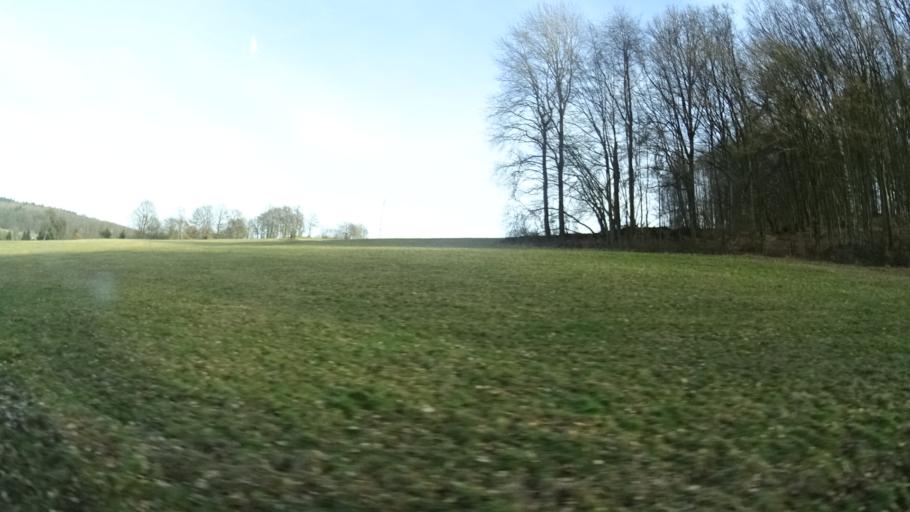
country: DE
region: Bavaria
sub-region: Regierungsbezirk Unterfranken
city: Bad Bruckenau
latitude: 50.3091
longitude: 9.7358
